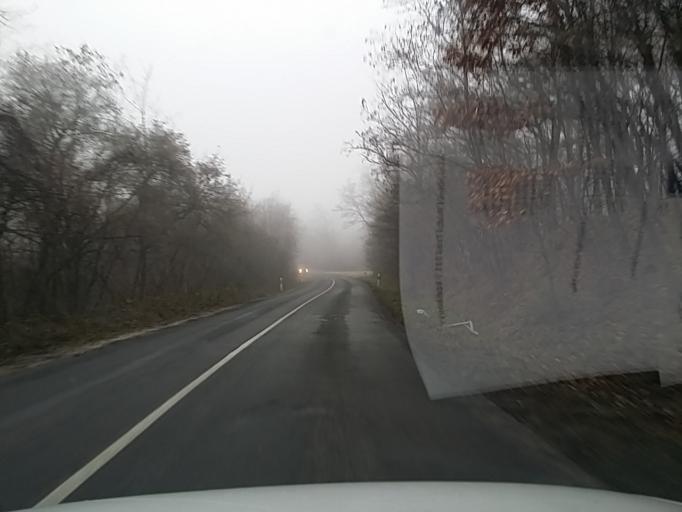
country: HU
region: Pest
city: Telki
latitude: 47.5370
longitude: 18.8502
